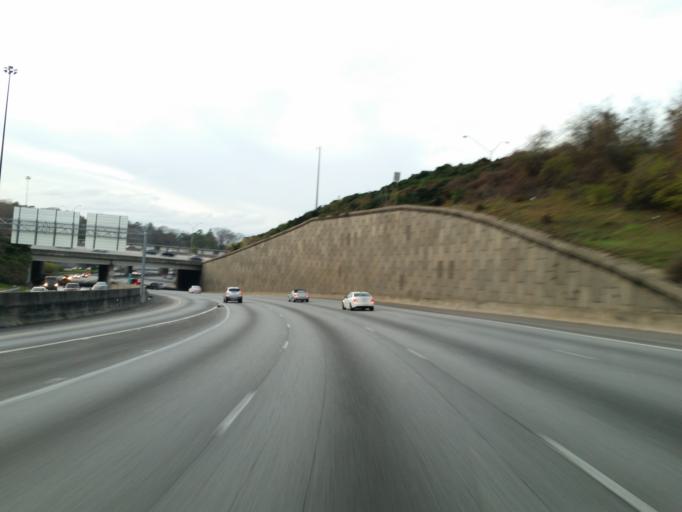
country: US
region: Georgia
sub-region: Fulton County
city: Atlanta
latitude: 33.7950
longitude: -84.3916
